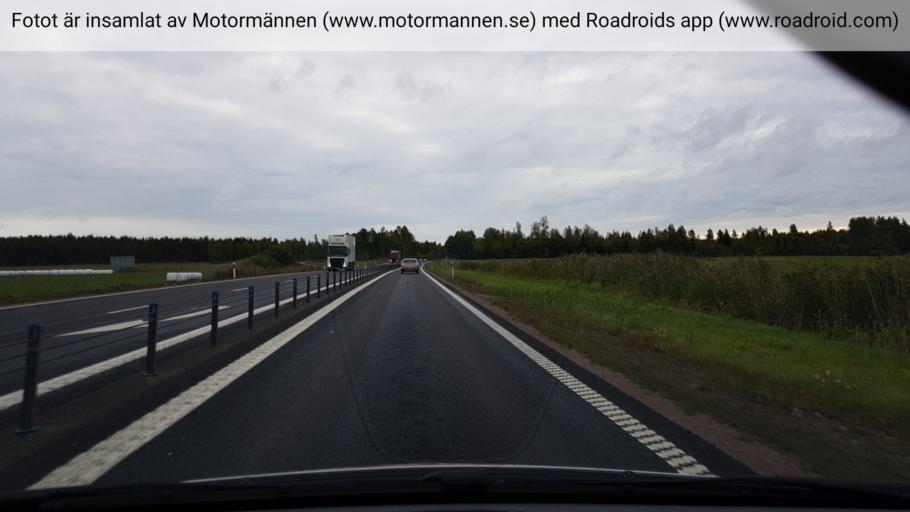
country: SE
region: Vaermland
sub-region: Karlstads Kommun
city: Skattkarr
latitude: 59.4150
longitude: 13.7448
